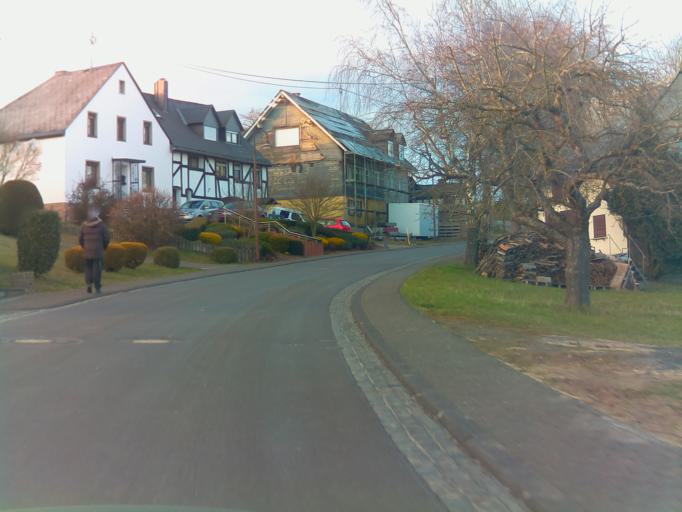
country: DE
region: Rheinland-Pfalz
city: Sulzbach
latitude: 49.8360
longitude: 7.3350
